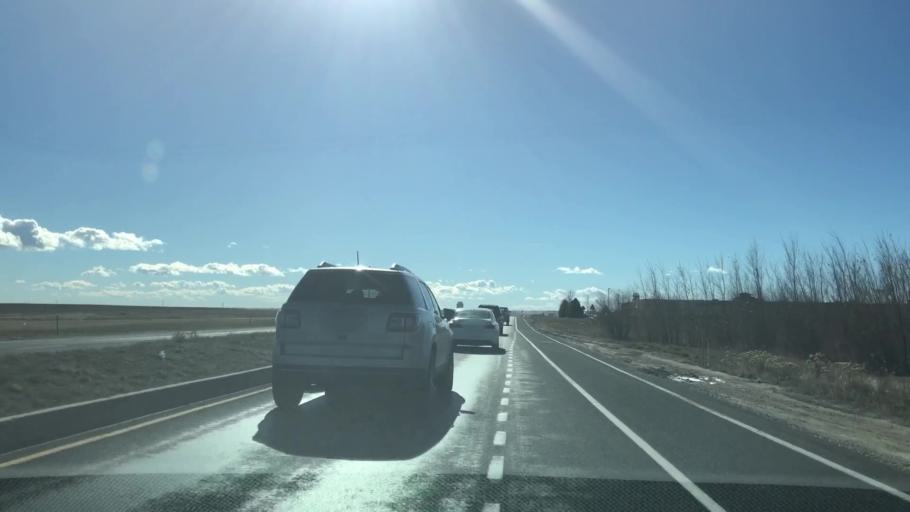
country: US
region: Colorado
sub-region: Weld County
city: Windsor
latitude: 40.4340
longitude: -104.9827
